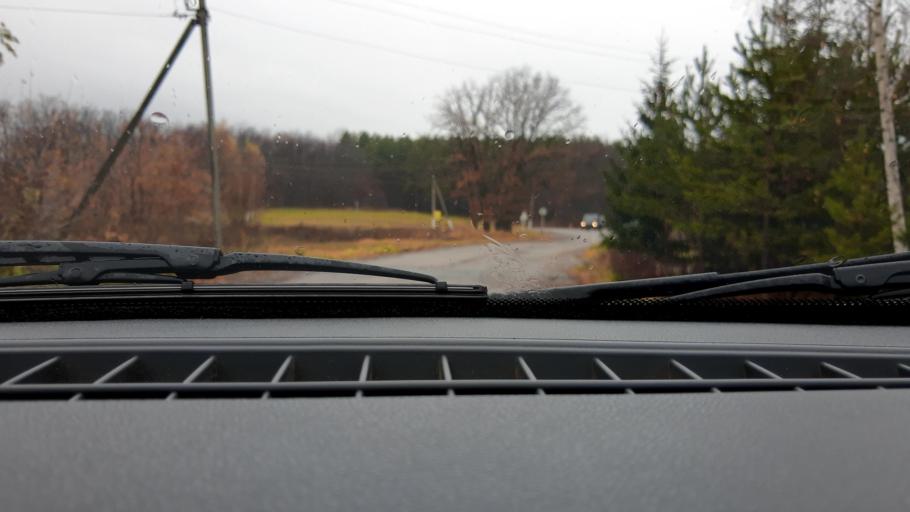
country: RU
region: Bashkortostan
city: Mikhaylovka
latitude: 54.8054
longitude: 55.8776
